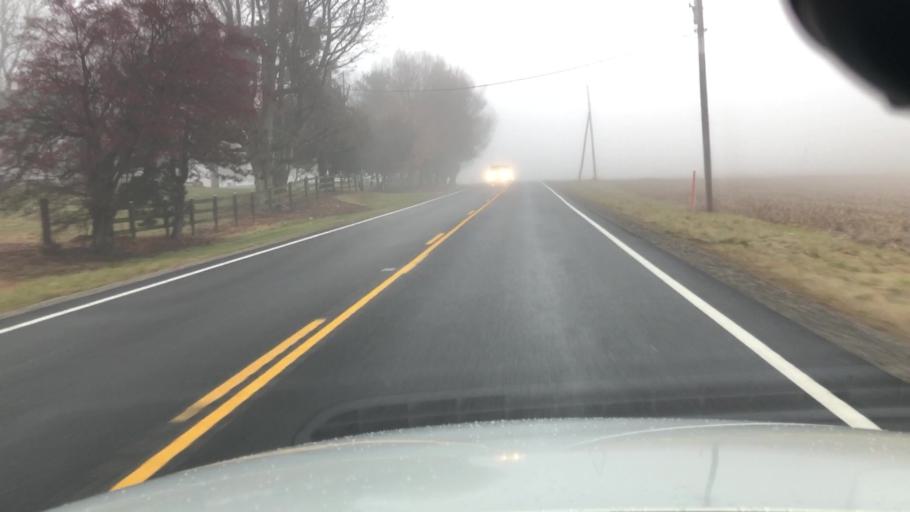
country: US
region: Ohio
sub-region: Logan County
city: Russells Point
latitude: 40.5685
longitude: -83.8453
